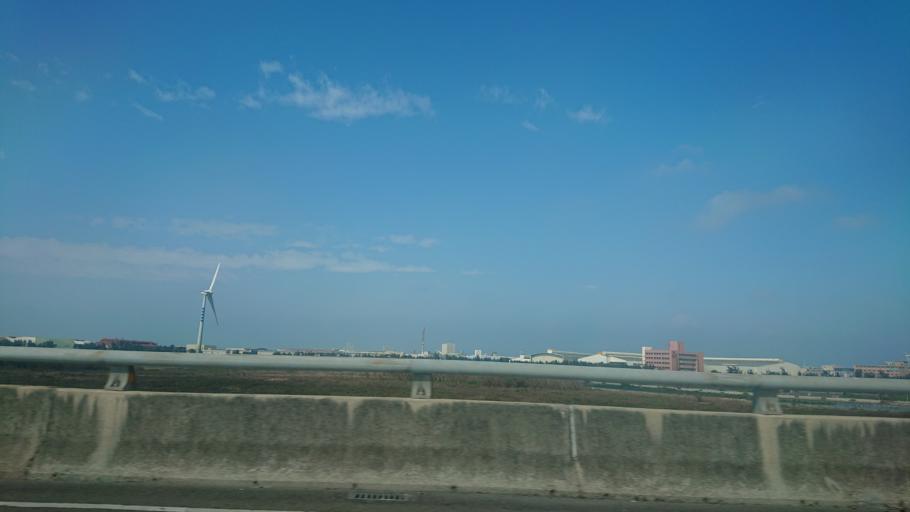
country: TW
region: Taiwan
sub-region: Changhua
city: Chang-hua
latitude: 24.0713
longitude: 120.4146
